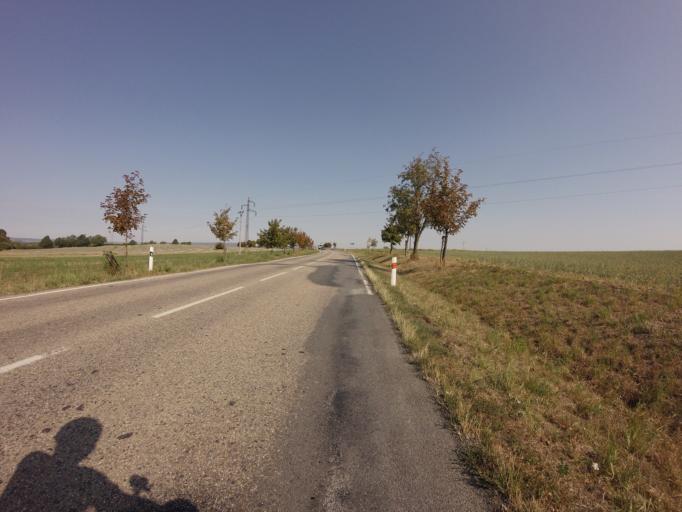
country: CZ
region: Central Bohemia
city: Porici nad Sazavou
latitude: 49.8067
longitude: 14.6501
